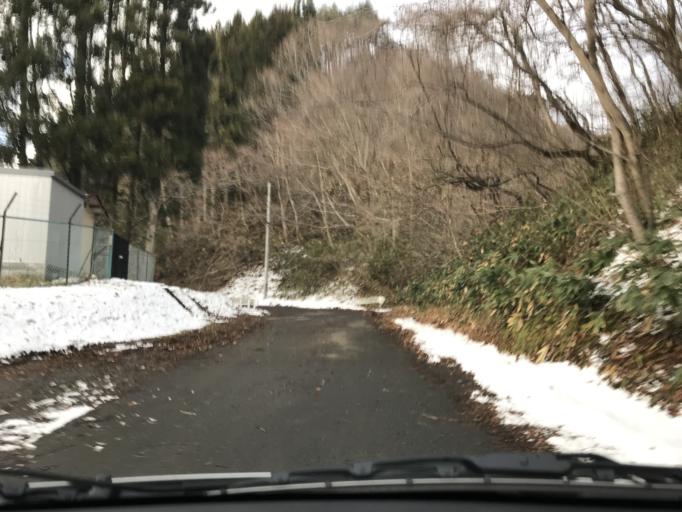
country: JP
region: Iwate
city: Ichinoseki
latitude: 39.0160
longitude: 140.9741
